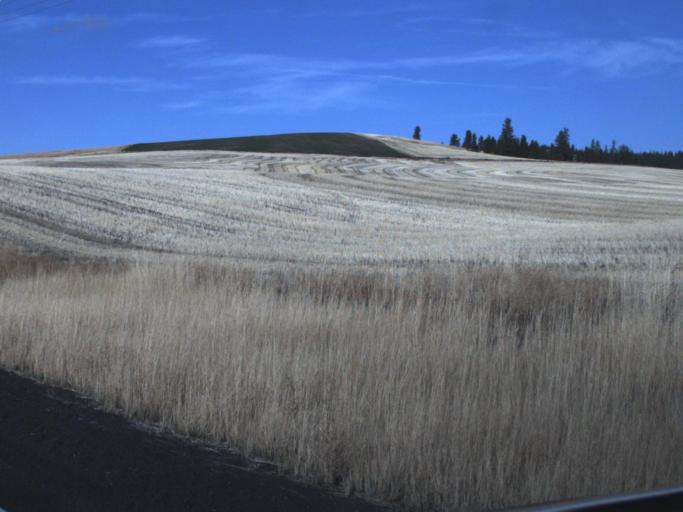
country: US
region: Washington
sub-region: Lincoln County
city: Davenport
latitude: 47.8271
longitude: -118.2048
